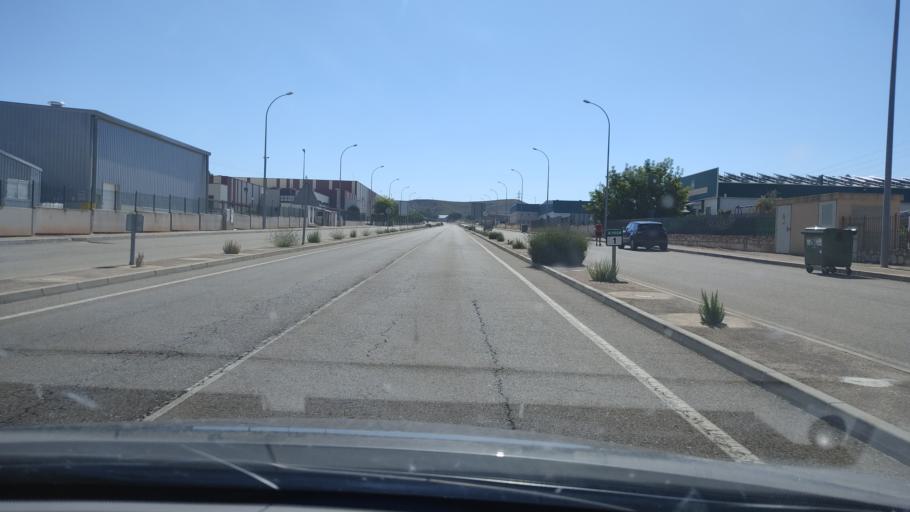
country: ES
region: Aragon
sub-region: Provincia de Teruel
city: Calamocha
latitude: 40.9175
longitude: -1.2824
